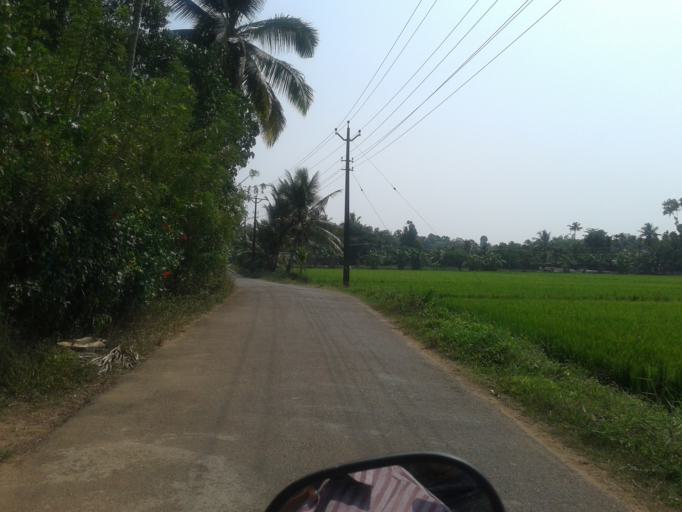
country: IN
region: Kerala
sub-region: Kottayam
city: Changanacheri
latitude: 9.4638
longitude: 76.4436
